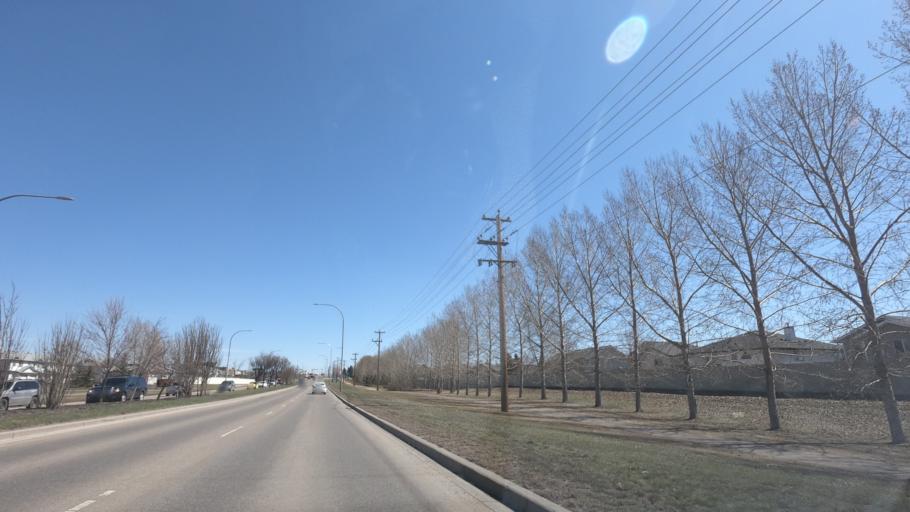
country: CA
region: Alberta
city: Airdrie
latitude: 51.2999
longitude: -114.0188
